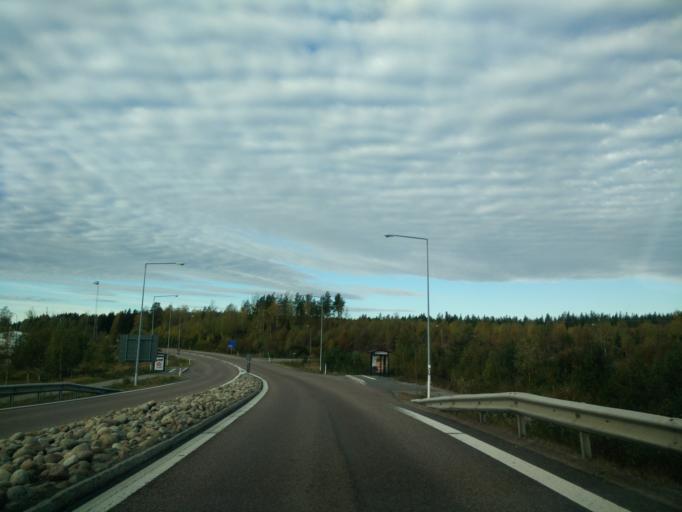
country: SE
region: Gaevleborg
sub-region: Soderhamns Kommun
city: Soderhamn
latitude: 61.2972
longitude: 17.0213
